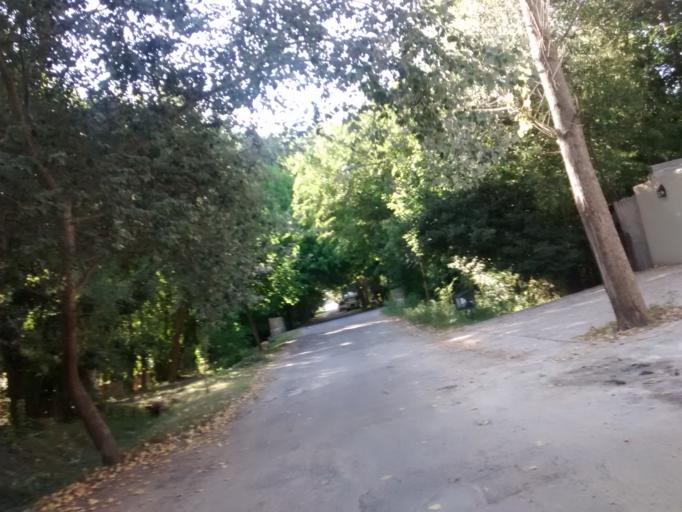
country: AR
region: Buenos Aires
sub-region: Partido de La Plata
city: La Plata
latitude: -34.8604
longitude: -58.0754
